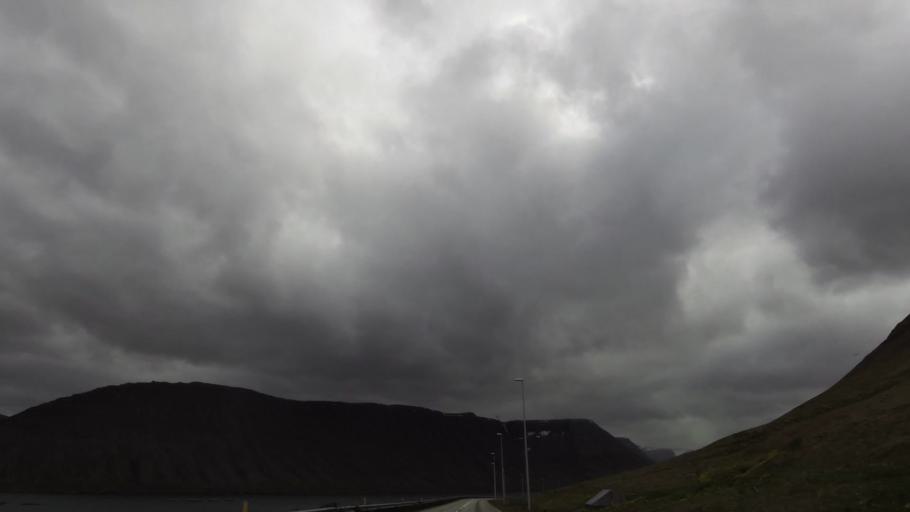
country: IS
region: Westfjords
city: Isafjoerdur
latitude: 66.1017
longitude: -23.1093
